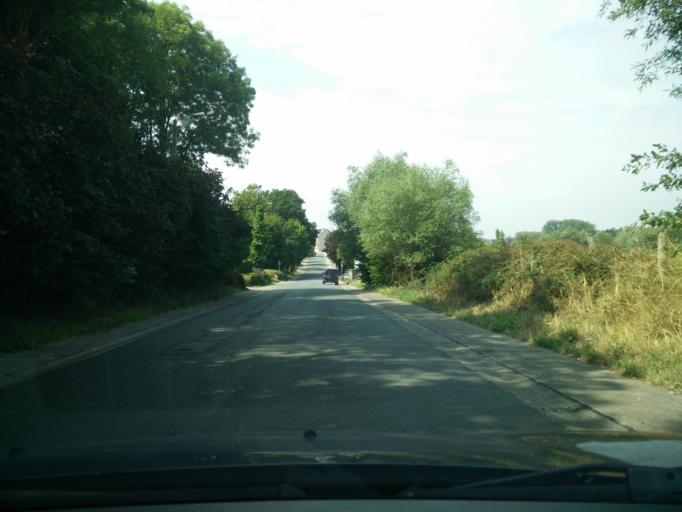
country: BE
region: Flanders
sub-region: Provincie Vlaams-Brabant
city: Halle
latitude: 50.7118
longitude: 4.2506
